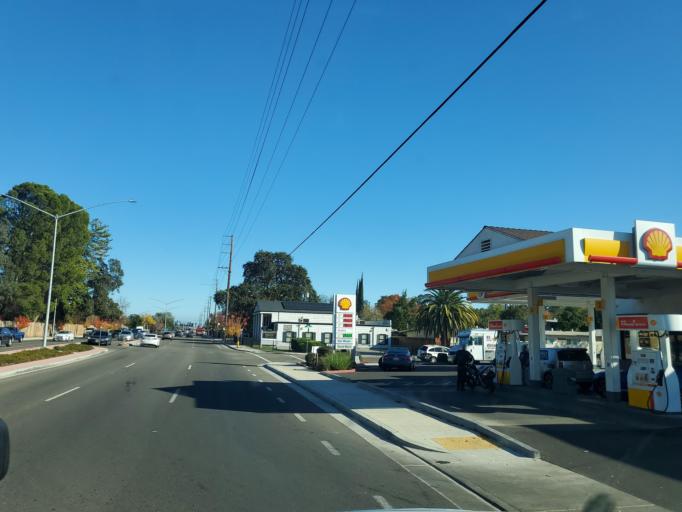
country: US
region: California
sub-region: San Joaquin County
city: Lincoln Village
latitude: 38.0209
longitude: -121.3339
